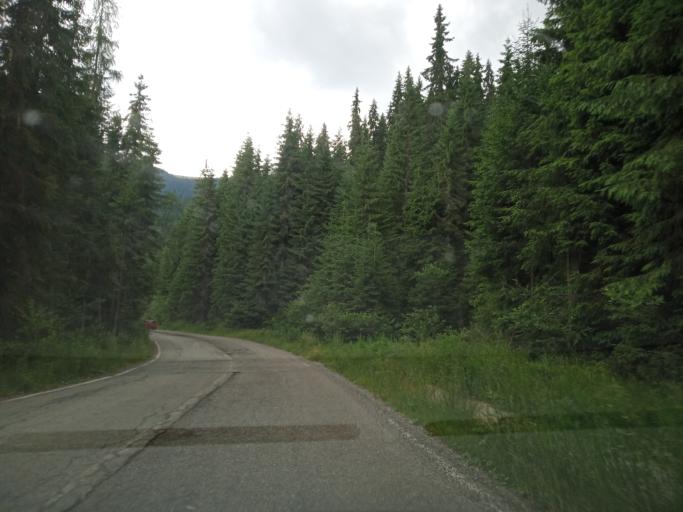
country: RO
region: Valcea
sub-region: Comuna Voineasa
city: Voineasa
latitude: 45.4147
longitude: 23.7241
